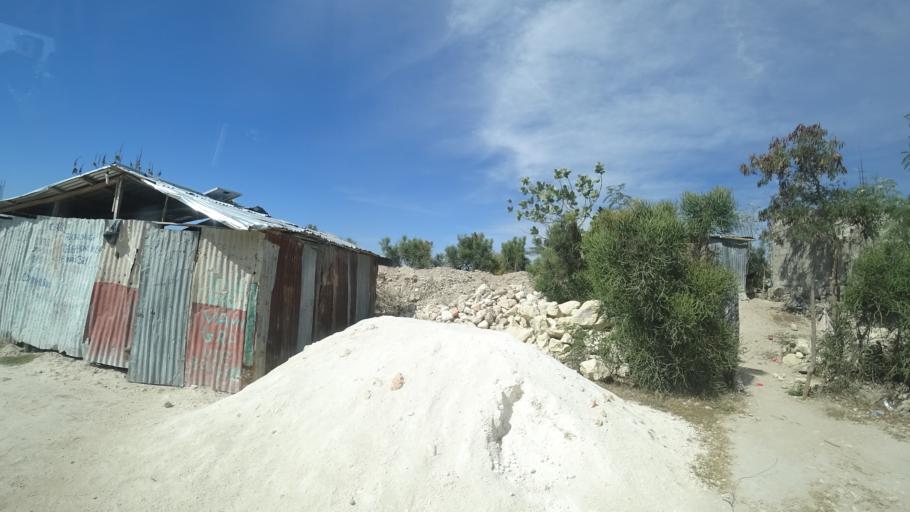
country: HT
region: Ouest
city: Croix des Bouquets
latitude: 18.6580
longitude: -72.2481
